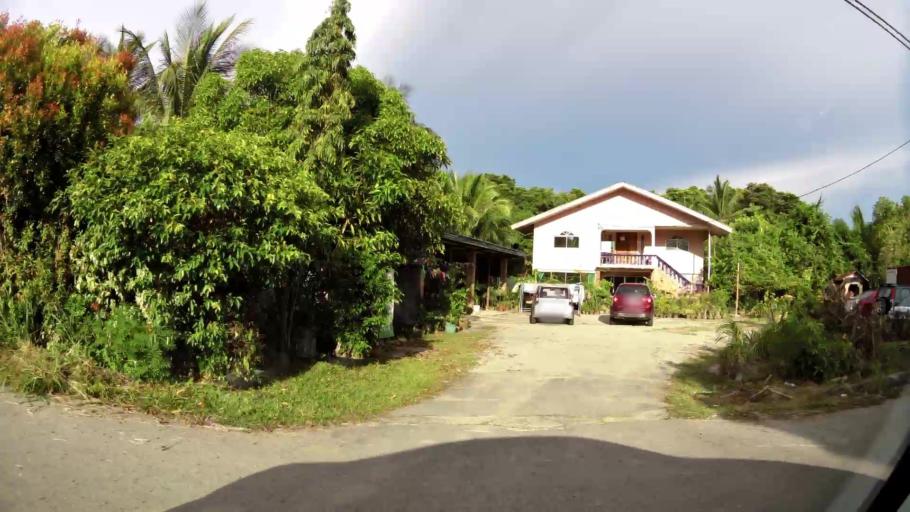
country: BN
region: Brunei and Muara
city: Bandar Seri Begawan
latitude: 4.9535
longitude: 115.0246
